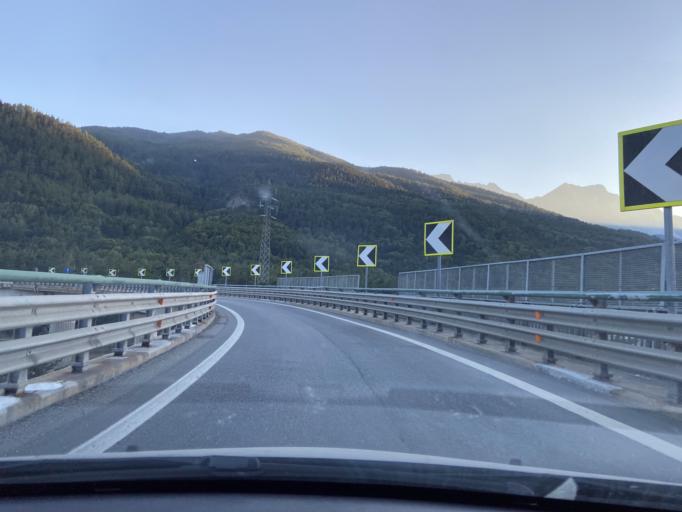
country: IT
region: Piedmont
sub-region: Provincia di Torino
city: Oulx
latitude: 45.0392
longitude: 6.8162
